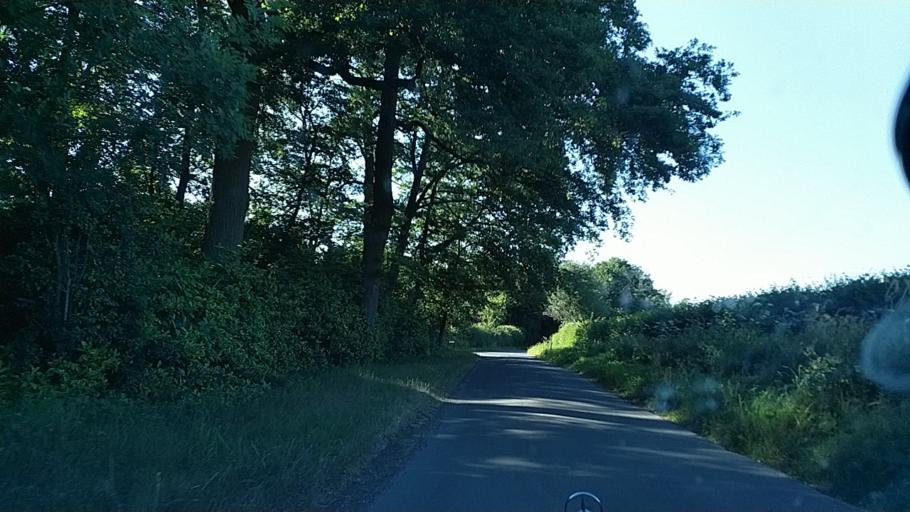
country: GB
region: England
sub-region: Warwickshire
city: Wroxall
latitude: 52.3190
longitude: -1.6448
